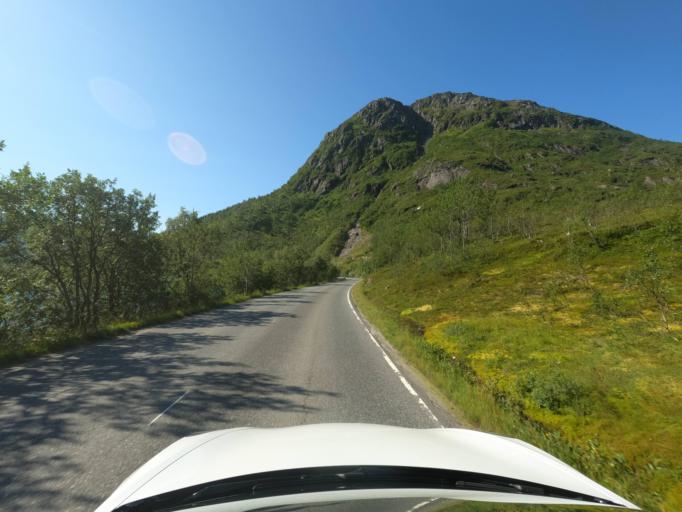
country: NO
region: Nordland
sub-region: Lodingen
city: Lodingen
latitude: 68.5583
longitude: 15.7494
